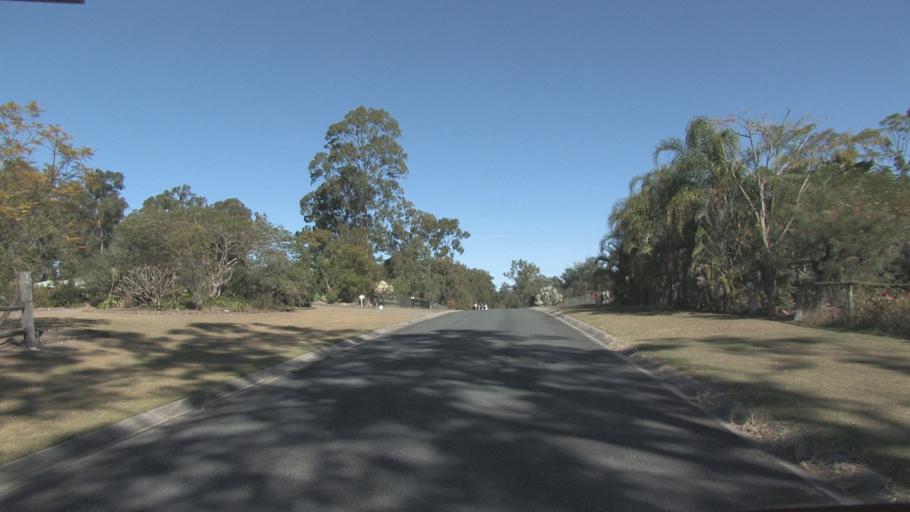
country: AU
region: Queensland
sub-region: Logan
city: North Maclean
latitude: -27.8199
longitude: 152.9452
